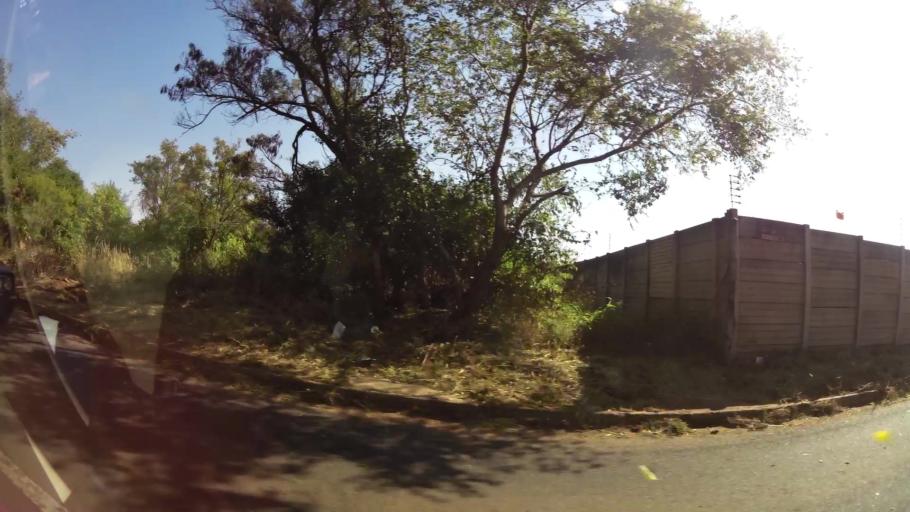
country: ZA
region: Gauteng
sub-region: City of Tshwane Metropolitan Municipality
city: Pretoria
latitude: -25.6689
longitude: 28.2551
